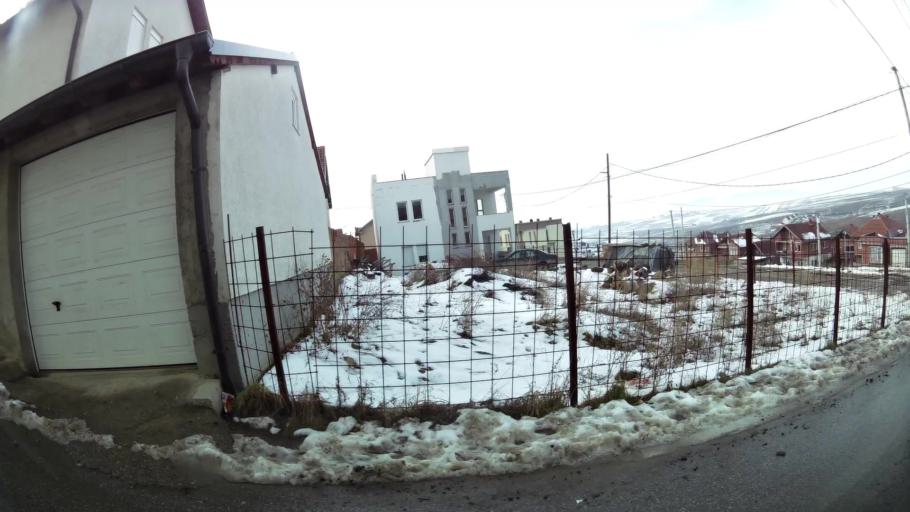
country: XK
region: Pristina
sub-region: Komuna e Prishtines
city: Pristina
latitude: 42.6774
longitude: 21.1549
